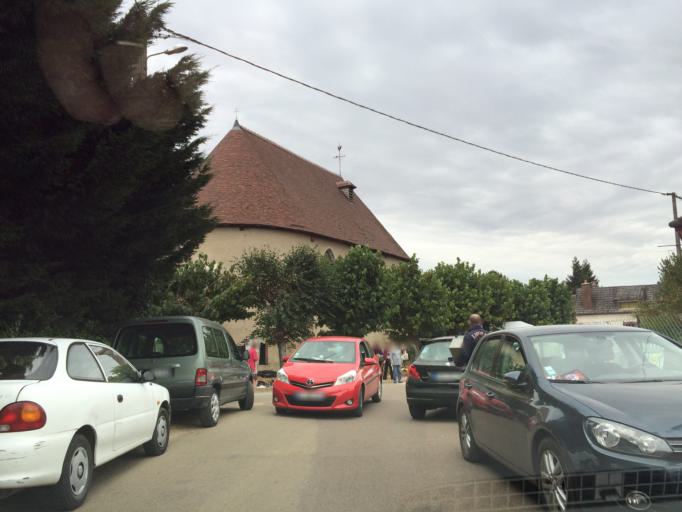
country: FR
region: Bourgogne
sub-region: Departement de l'Yonne
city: Aillant-sur-Tholon
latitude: 47.8492
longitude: 3.2673
